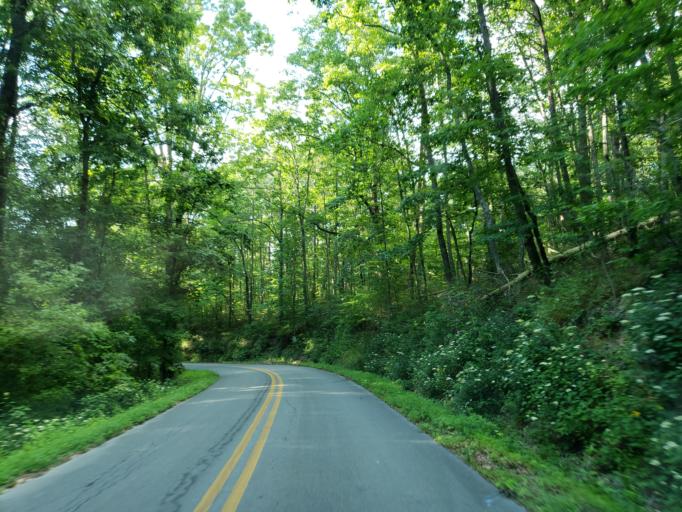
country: US
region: Georgia
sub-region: Haralson County
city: Buchanan
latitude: 33.9006
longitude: -85.2726
